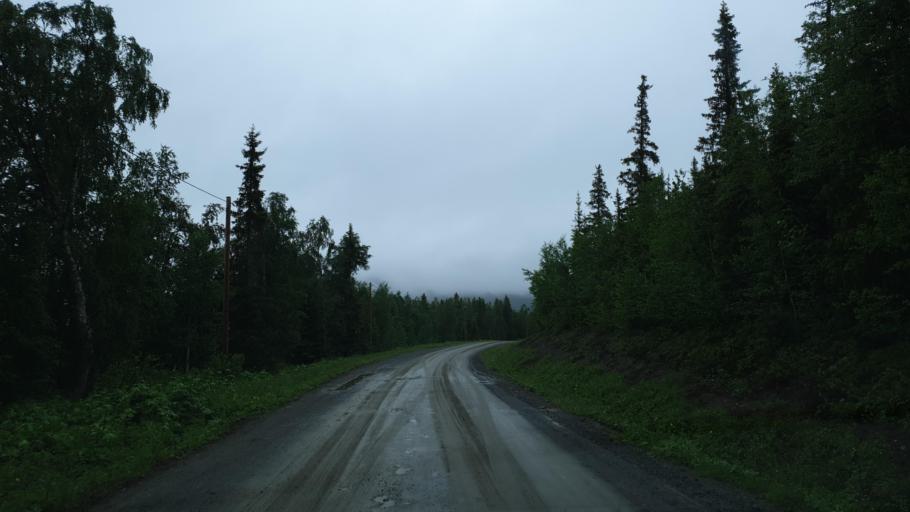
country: SE
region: Vaesterbotten
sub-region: Vilhelmina Kommun
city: Sjoberg
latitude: 65.3311
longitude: 15.8678
